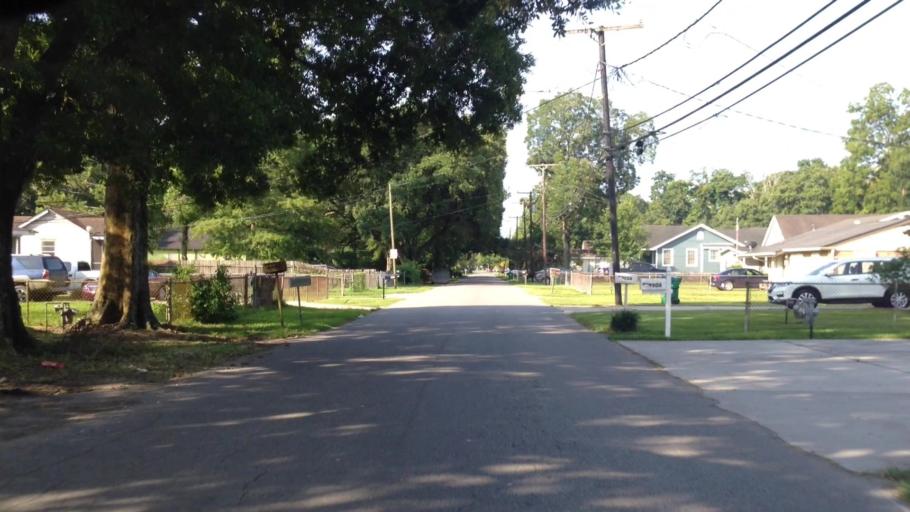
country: US
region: Louisiana
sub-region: Jefferson Parish
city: Bridge City
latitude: 29.9359
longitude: -90.1572
